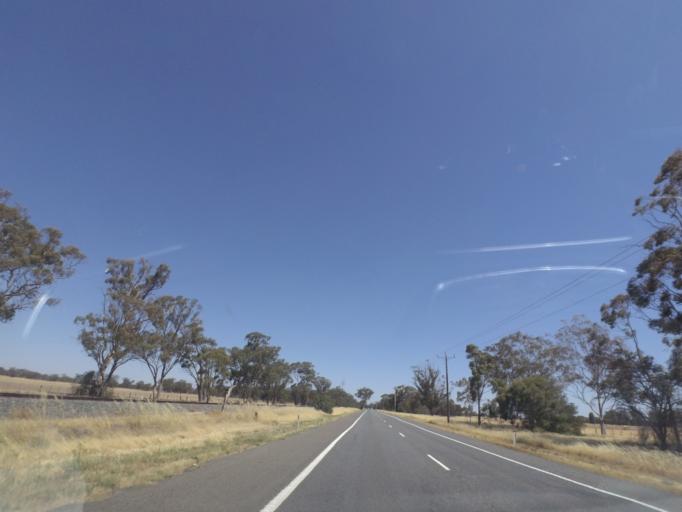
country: AU
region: Victoria
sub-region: Greater Shepparton
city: Shepparton
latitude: -36.2230
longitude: 145.4318
